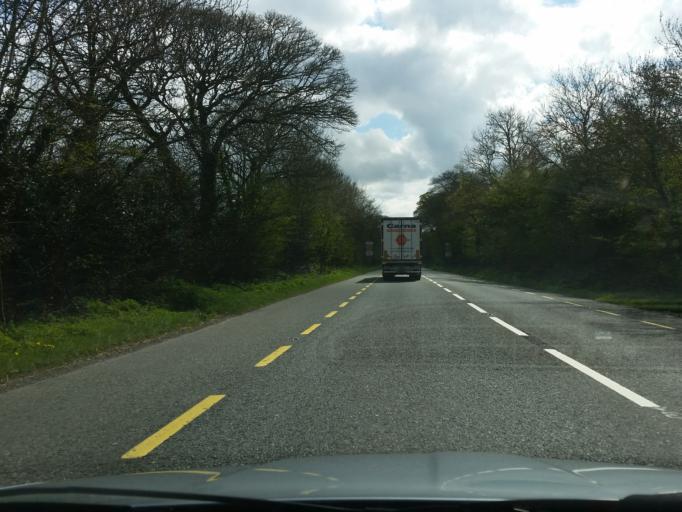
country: IE
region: Leinster
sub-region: An Mhi
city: Ashbourne
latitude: 53.5343
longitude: -6.4225
